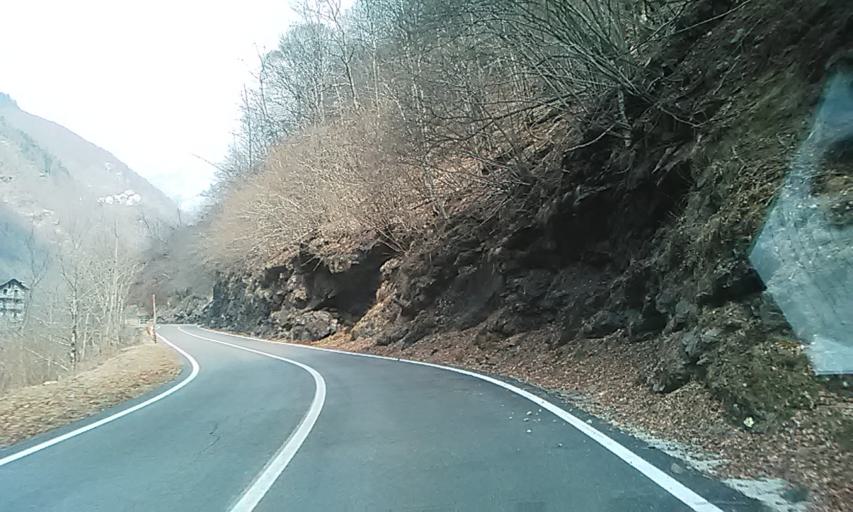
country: IT
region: Piedmont
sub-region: Provincia di Vercelli
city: Rimella
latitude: 45.9017
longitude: 8.1802
